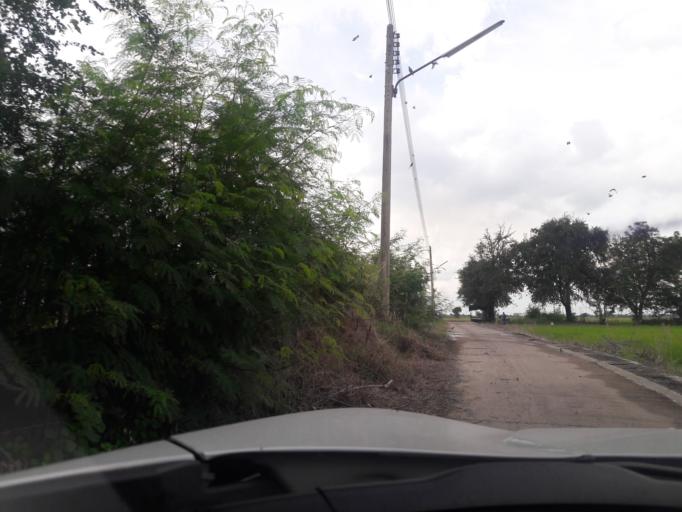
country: TH
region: Lop Buri
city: Ban Mi
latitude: 15.0492
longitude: 100.5350
